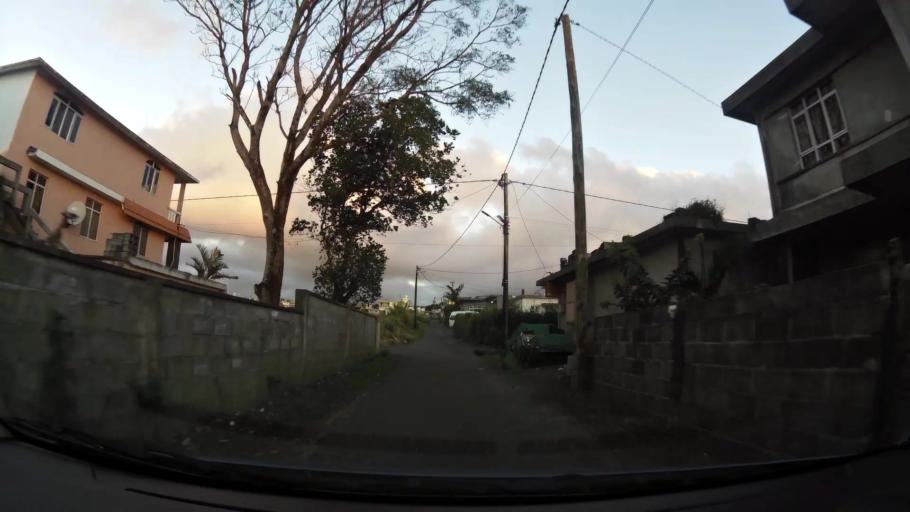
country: MU
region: Plaines Wilhems
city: Curepipe
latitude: -20.2990
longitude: 57.5249
